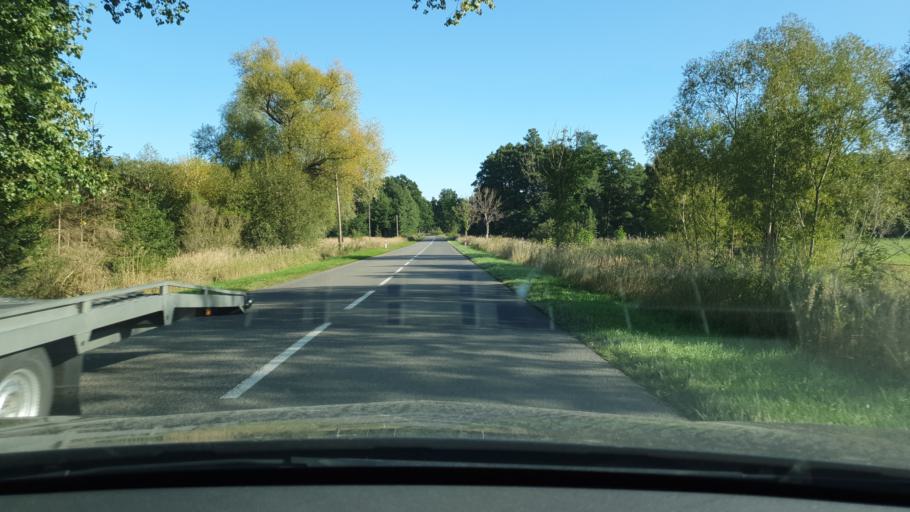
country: PL
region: West Pomeranian Voivodeship
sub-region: Powiat goleniowski
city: Przybiernow
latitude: 53.8303
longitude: 14.7753
